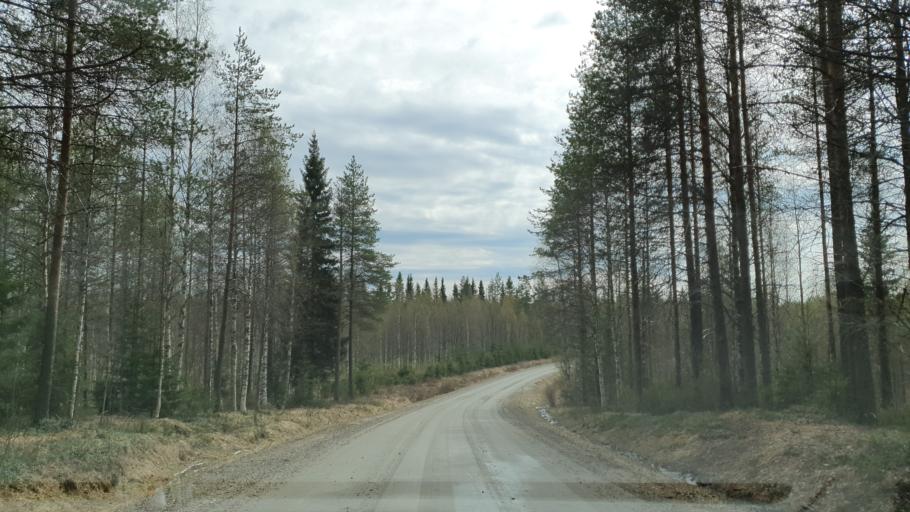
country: FI
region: Kainuu
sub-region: Kehys-Kainuu
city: Kuhmo
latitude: 64.1293
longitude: 29.9772
